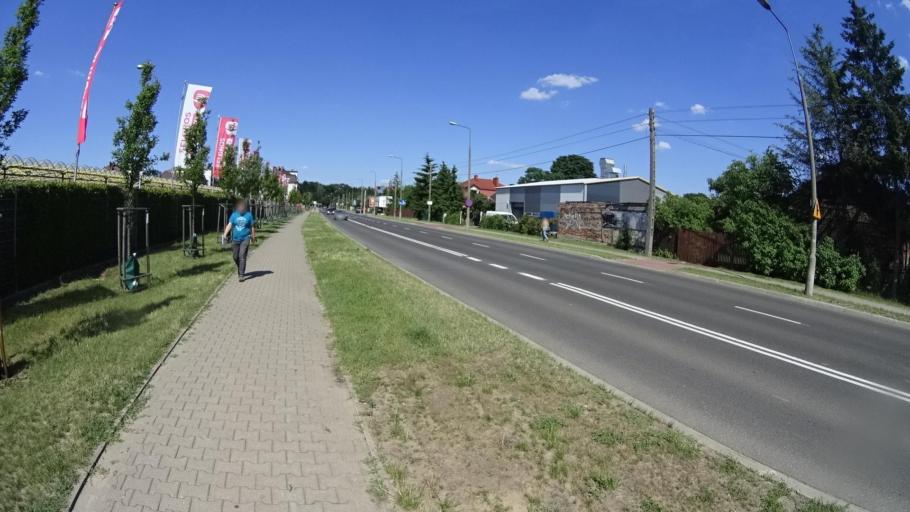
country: PL
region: Masovian Voivodeship
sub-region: Warszawa
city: Bialoleka
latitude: 52.3451
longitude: 20.9543
